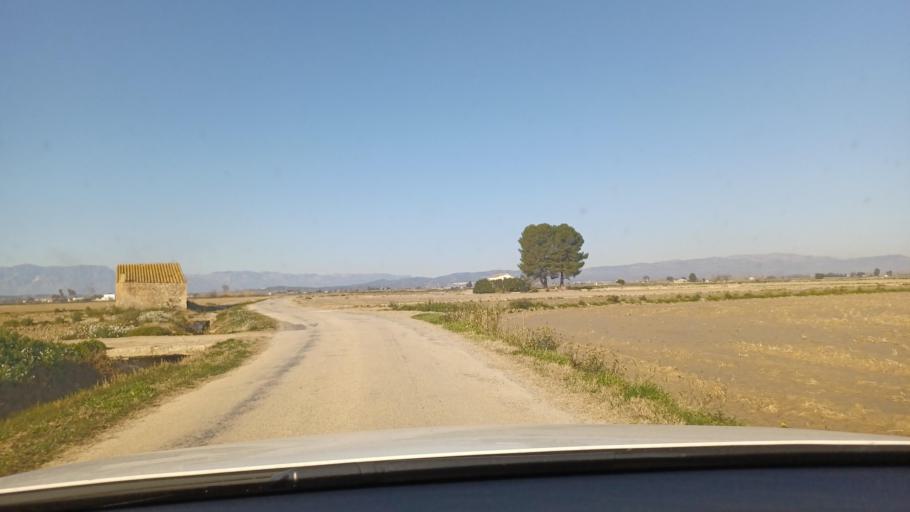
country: ES
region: Catalonia
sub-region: Provincia de Tarragona
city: Deltebre
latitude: 40.6956
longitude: 0.6495
